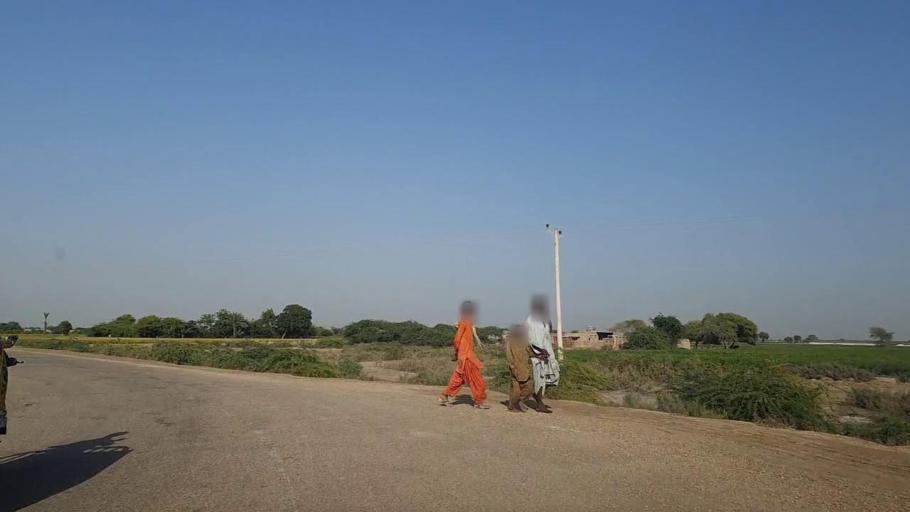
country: PK
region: Sindh
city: Mirpur Batoro
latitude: 24.5805
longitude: 68.3970
